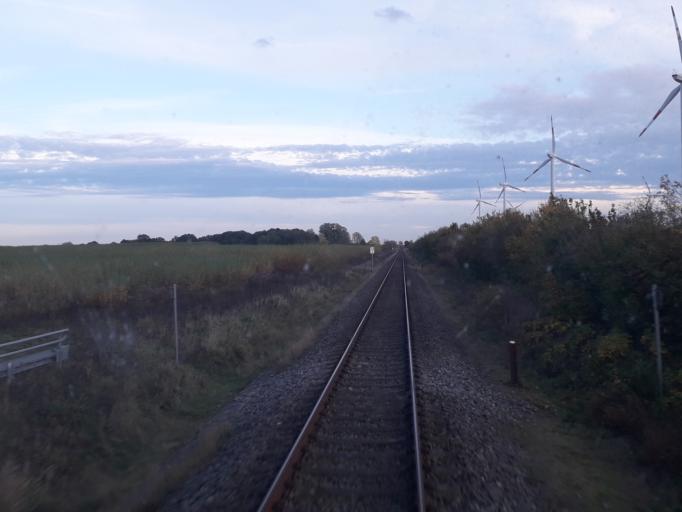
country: DE
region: Brandenburg
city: Walsleben
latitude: 52.9414
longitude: 12.6966
